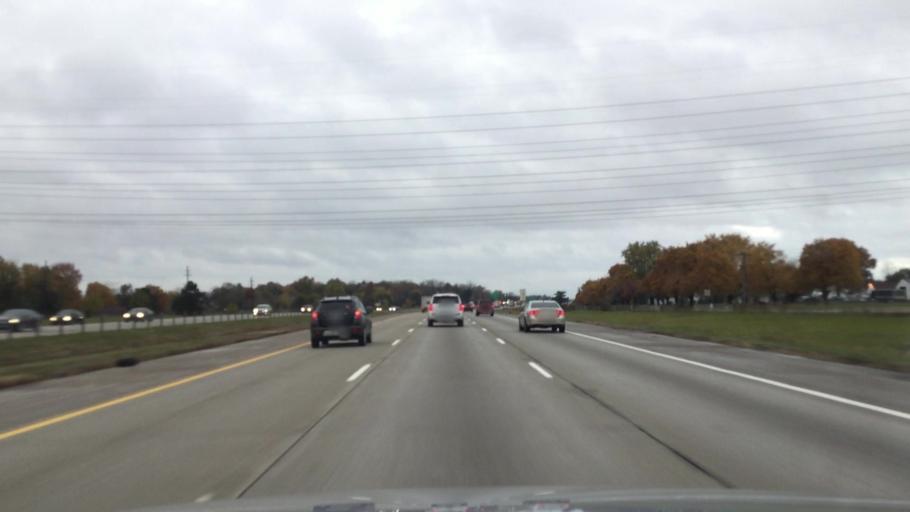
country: US
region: Michigan
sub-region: Wayne County
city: Belleville
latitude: 42.2209
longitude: -83.4529
